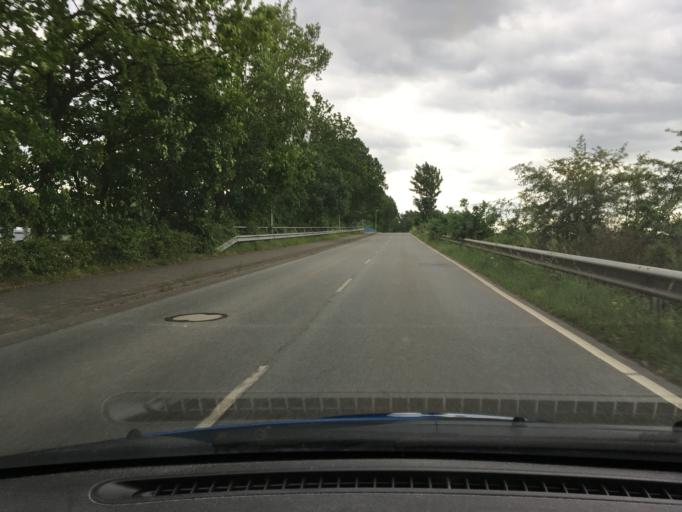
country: DE
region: Lower Saxony
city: Sittensen
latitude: 53.2914
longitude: 9.4984
